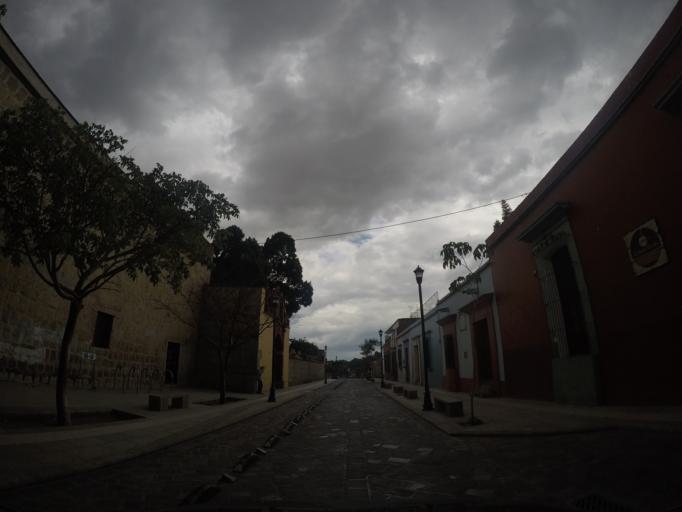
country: MX
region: Oaxaca
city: Oaxaca de Juarez
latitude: 17.0675
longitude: -96.7245
